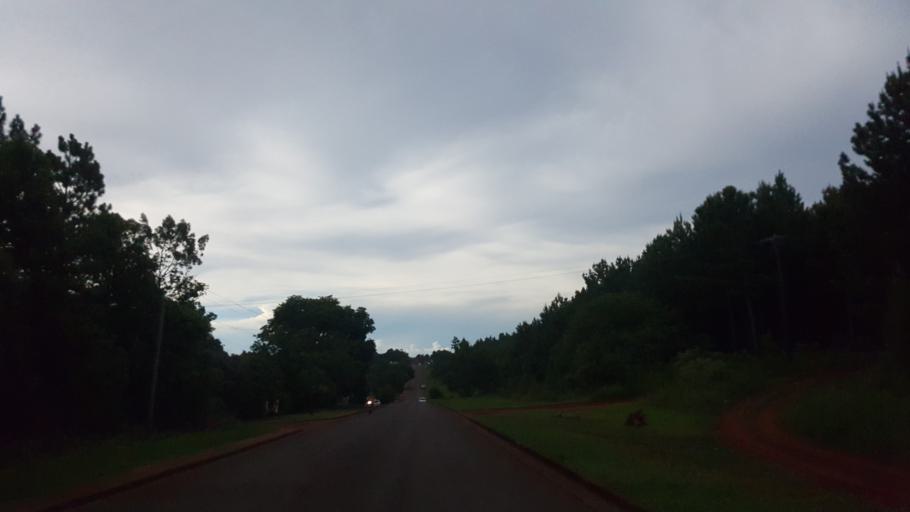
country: AR
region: Misiones
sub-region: Departamento de San Ignacio
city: San Ignacio
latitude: -27.2645
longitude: -55.5275
